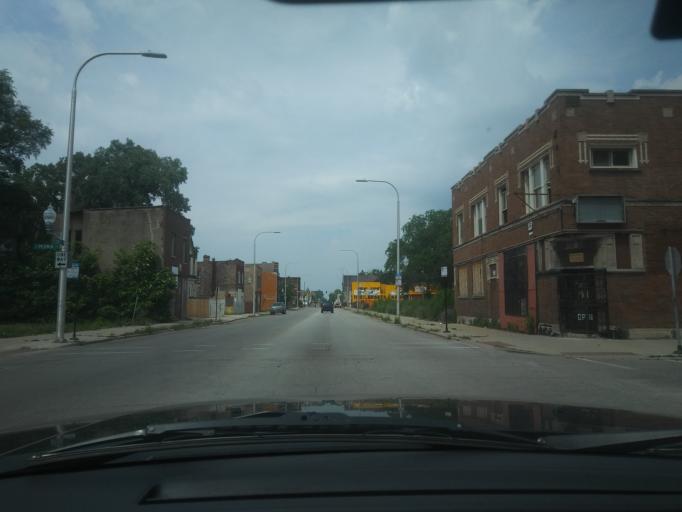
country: US
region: Illinois
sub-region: Cook County
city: Chicago
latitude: 41.7870
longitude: -87.6473
